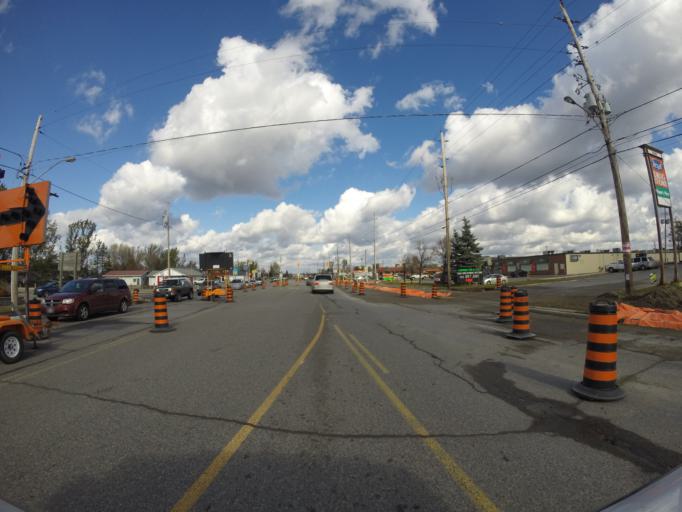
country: CA
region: Ontario
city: Greater Sudbury
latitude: 46.6125
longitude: -81.0074
